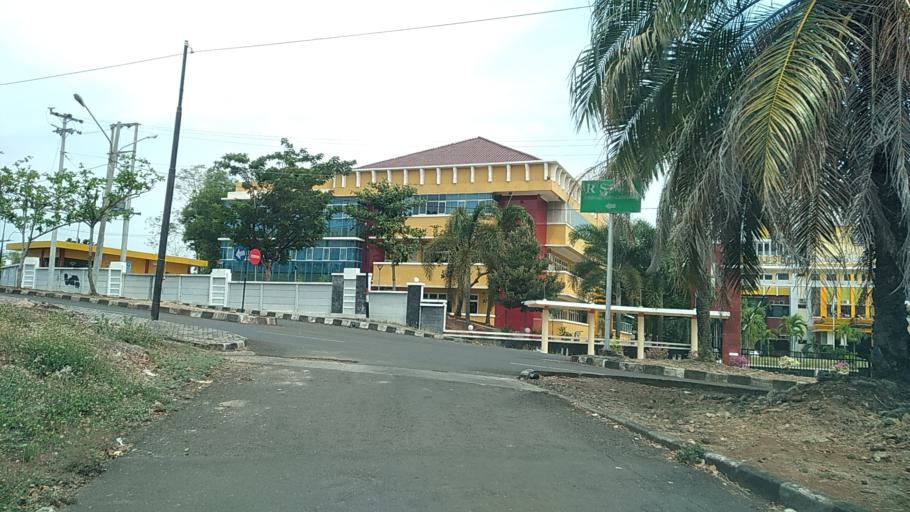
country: ID
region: Central Java
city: Semarang
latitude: -7.0459
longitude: 110.4414
